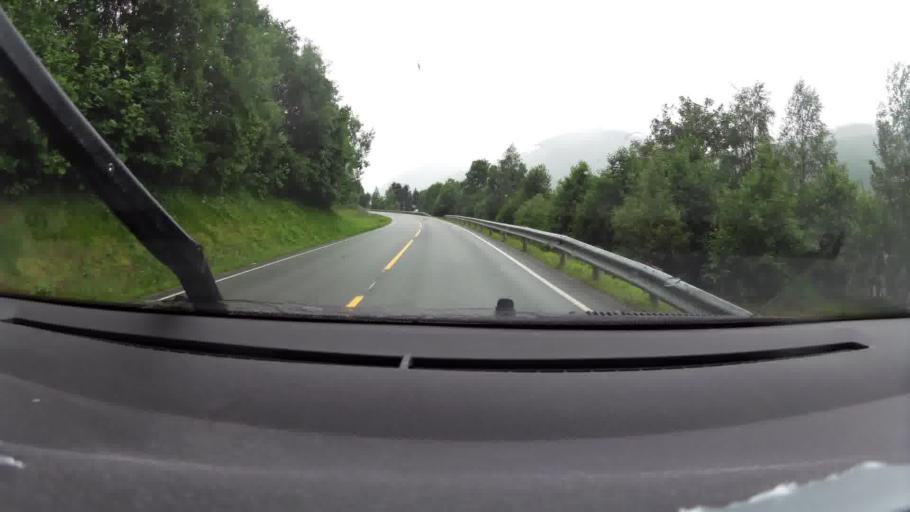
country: NO
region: More og Romsdal
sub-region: Gjemnes
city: Batnfjordsora
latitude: 62.9108
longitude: 7.7204
